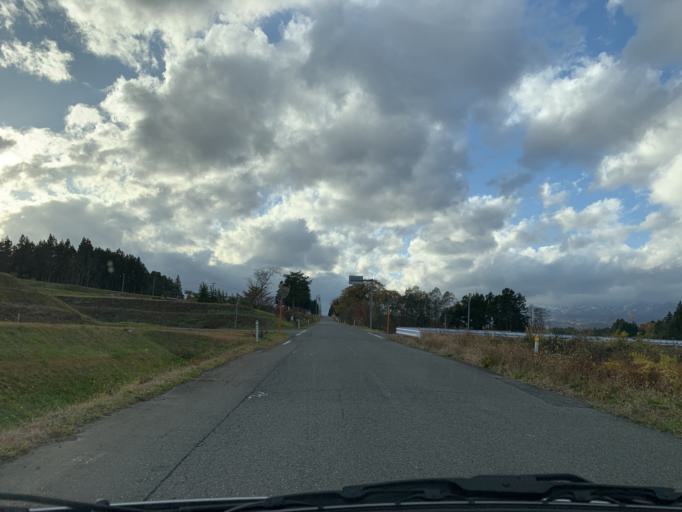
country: JP
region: Iwate
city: Mizusawa
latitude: 39.1085
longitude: 141.0246
